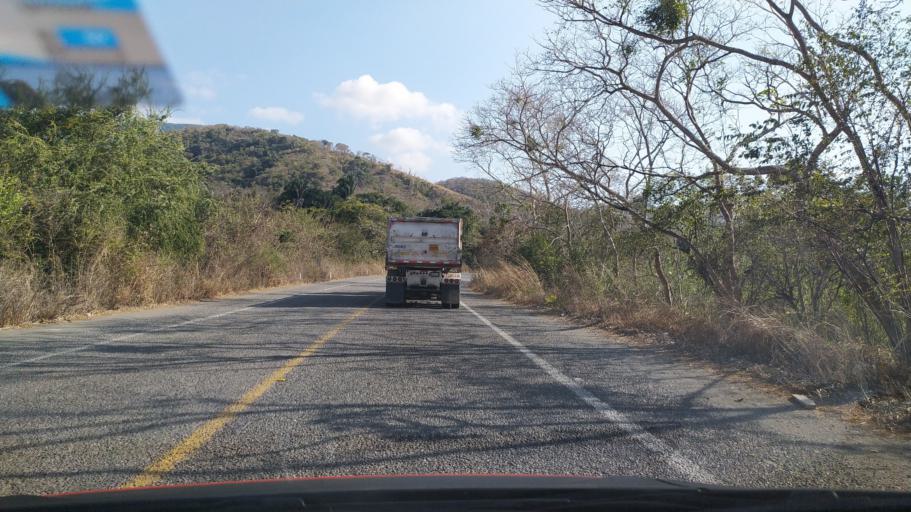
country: MX
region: Michoacan
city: Coahuayana Viejo
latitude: 18.6376
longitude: -103.6675
